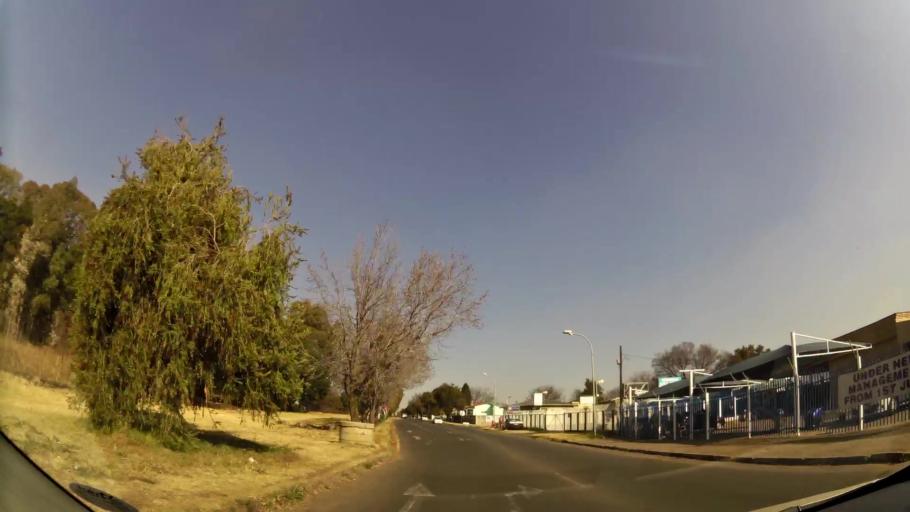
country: ZA
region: Gauteng
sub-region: West Rand District Municipality
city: Randfontein
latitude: -26.1677
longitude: 27.6890
